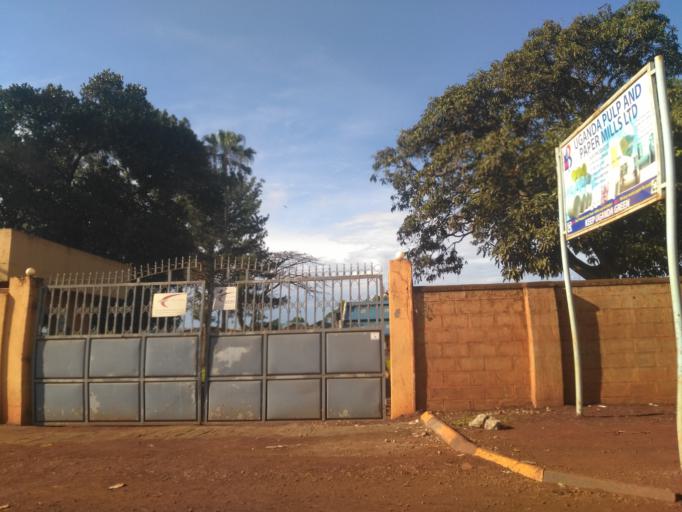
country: UG
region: Eastern Region
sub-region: Jinja District
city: Jinja
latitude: 0.4545
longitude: 33.1879
